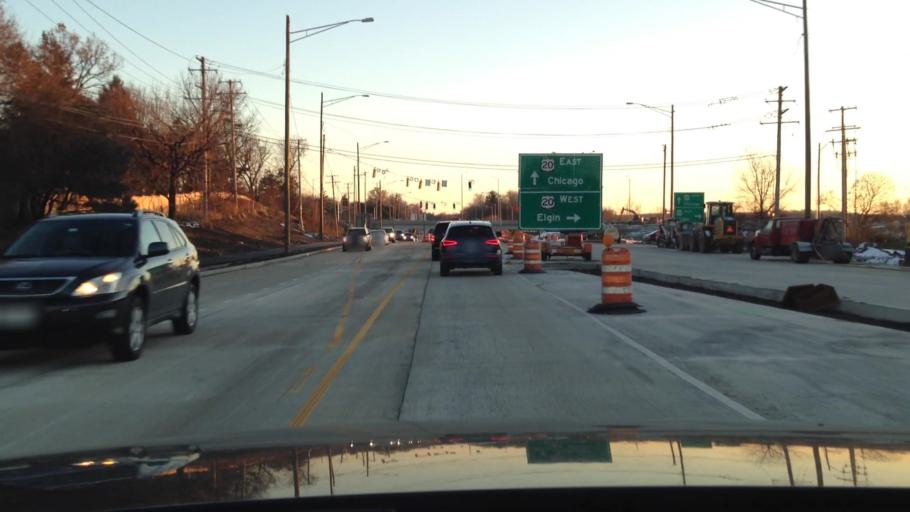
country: US
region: Illinois
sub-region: Cook County
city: Bartlett
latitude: 42.0110
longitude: -88.2032
